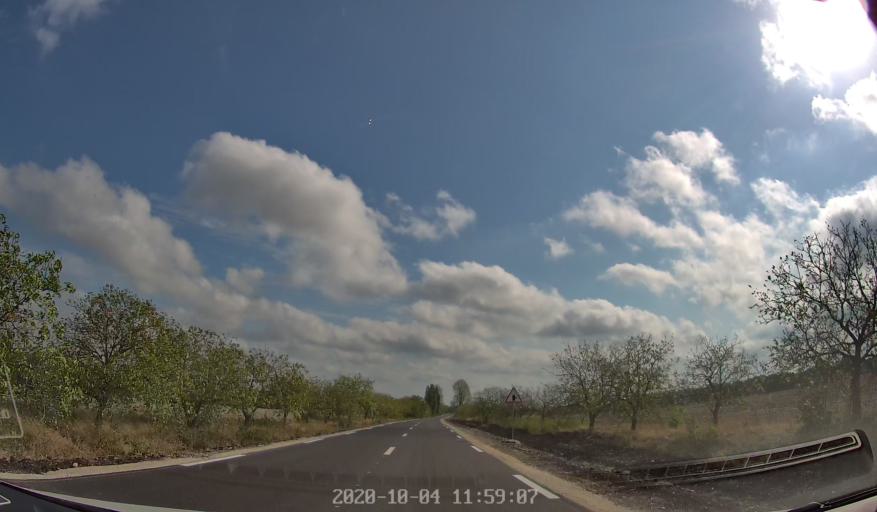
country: MD
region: Rezina
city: Saharna
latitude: 47.6330
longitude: 28.8448
